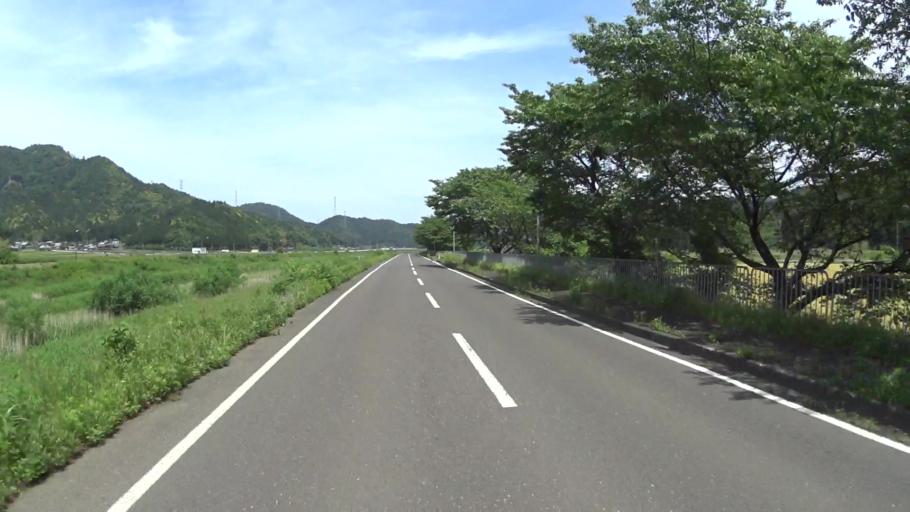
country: JP
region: Fukui
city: Obama
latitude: 35.4531
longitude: 135.5755
